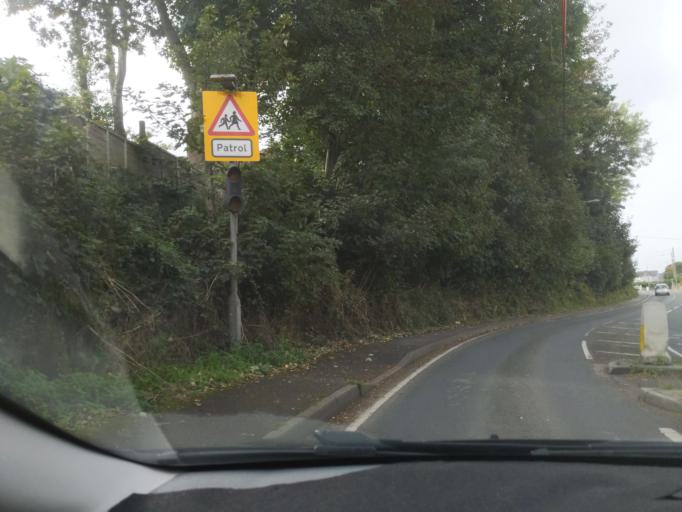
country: GB
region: England
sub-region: Cornwall
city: Par
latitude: 50.3499
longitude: -4.7201
